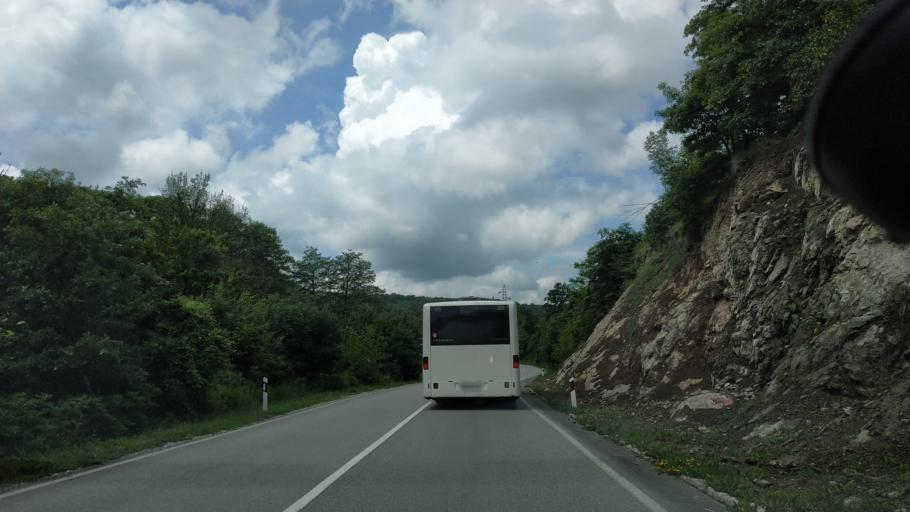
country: RS
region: Central Serbia
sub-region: Borski Okrug
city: Bor
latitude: 44.0558
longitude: 22.0615
